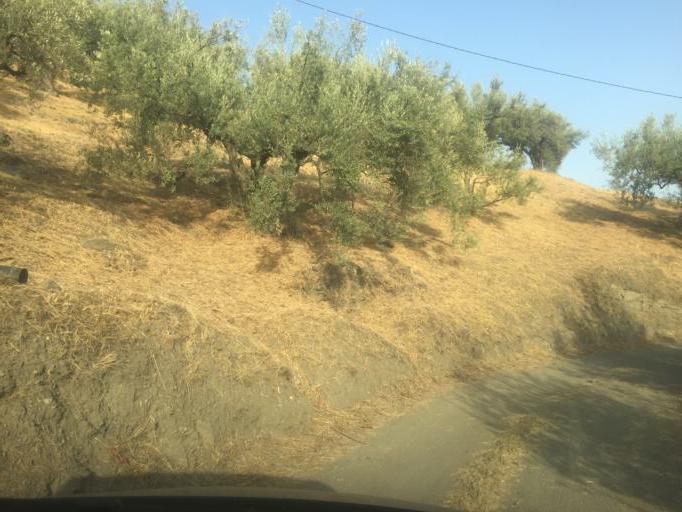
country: ES
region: Andalusia
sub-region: Provincia de Malaga
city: Competa
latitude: 36.8080
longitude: -3.9364
